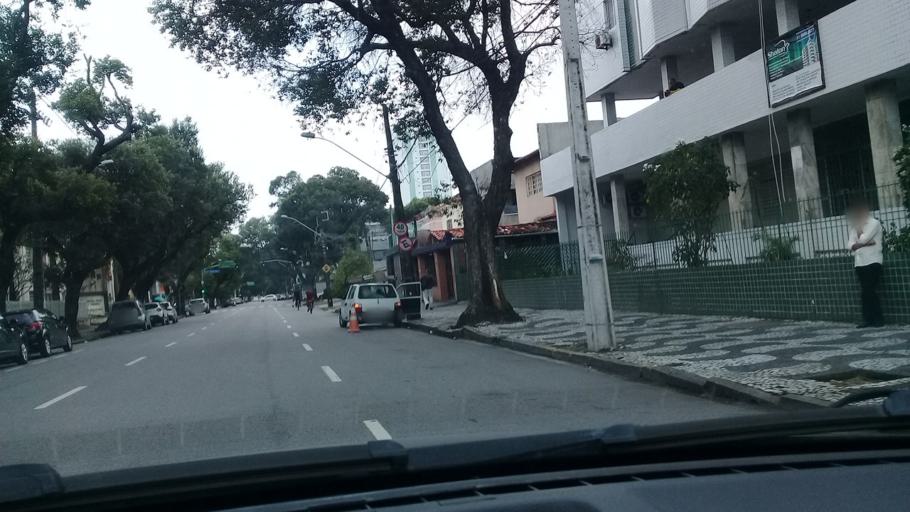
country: BR
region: Pernambuco
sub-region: Recife
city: Recife
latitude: -8.0550
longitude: -34.8824
